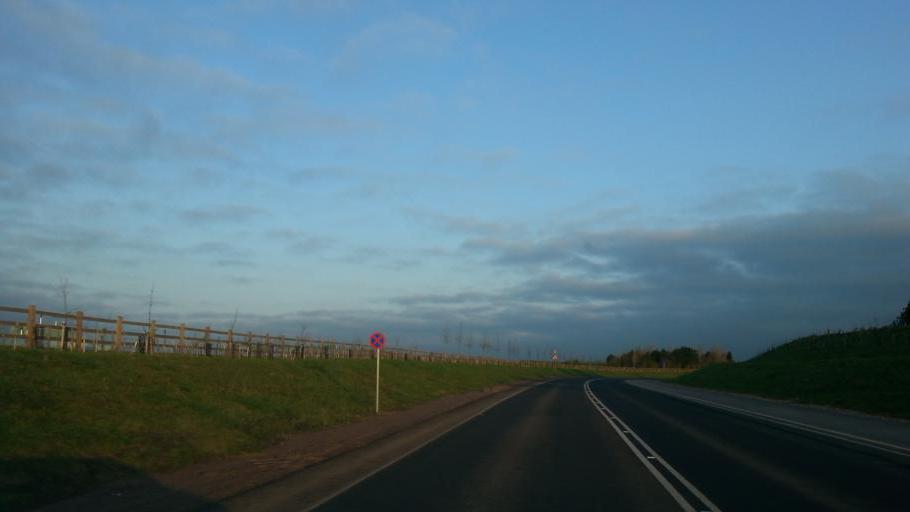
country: GB
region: England
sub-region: Nottinghamshire
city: Newark on Trent
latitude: 53.0460
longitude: -0.7934
